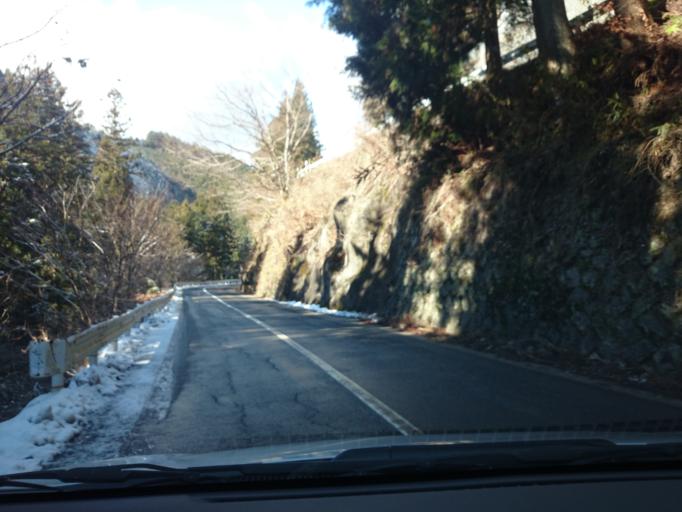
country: JP
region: Gifu
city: Gujo
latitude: 35.7472
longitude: 136.9747
